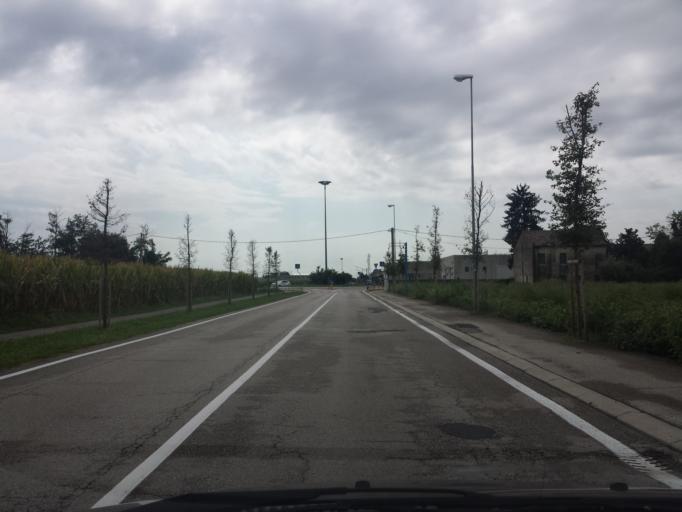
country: IT
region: Veneto
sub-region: Provincia di Padova
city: Galliera Veneta
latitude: 45.6726
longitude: 11.8166
